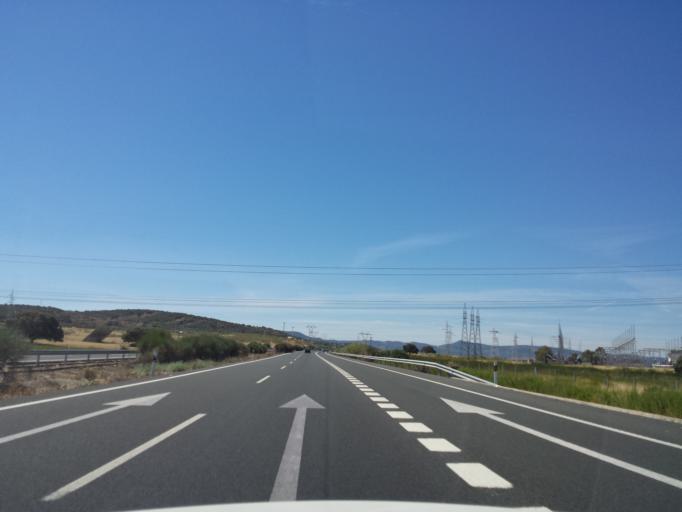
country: ES
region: Extremadura
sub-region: Provincia de Caceres
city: Almaraz
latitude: 39.8242
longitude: -5.6602
